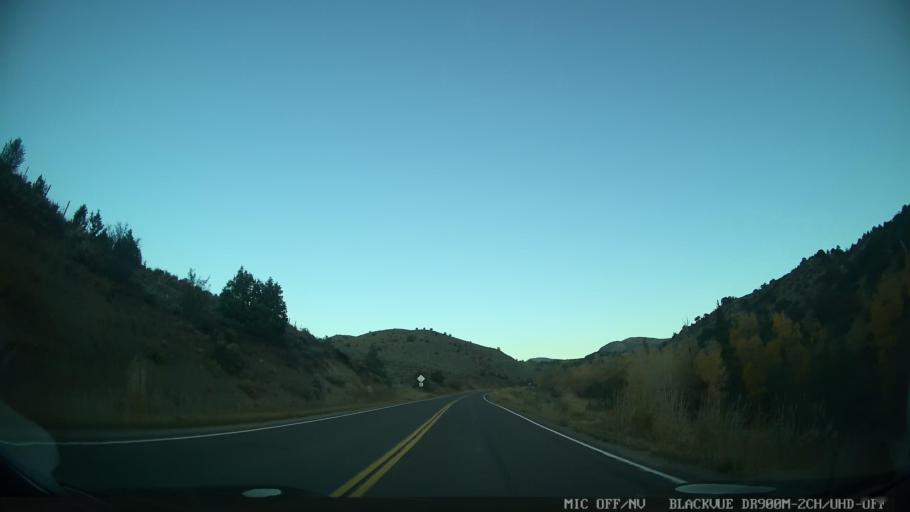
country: US
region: Colorado
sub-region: Eagle County
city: Edwards
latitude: 39.7599
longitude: -106.6735
